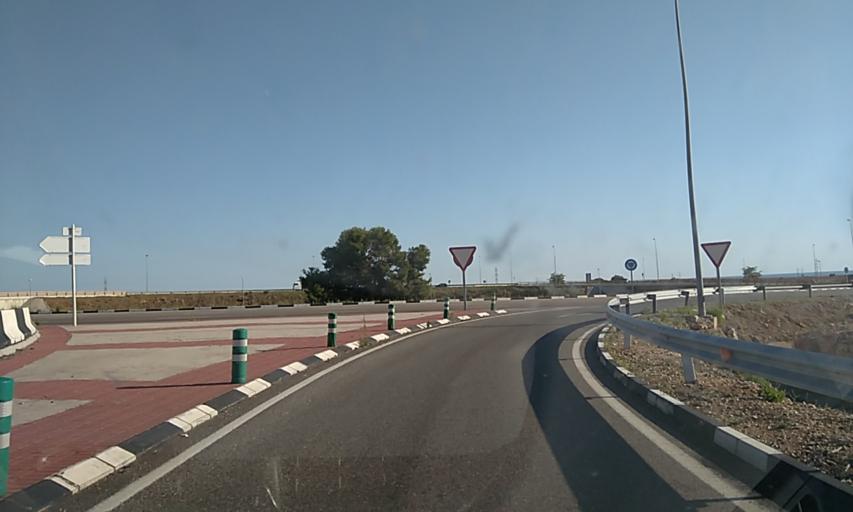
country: ES
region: Valencia
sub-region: Provincia de Castello
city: Torreblanca
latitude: 40.2288
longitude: 0.2128
